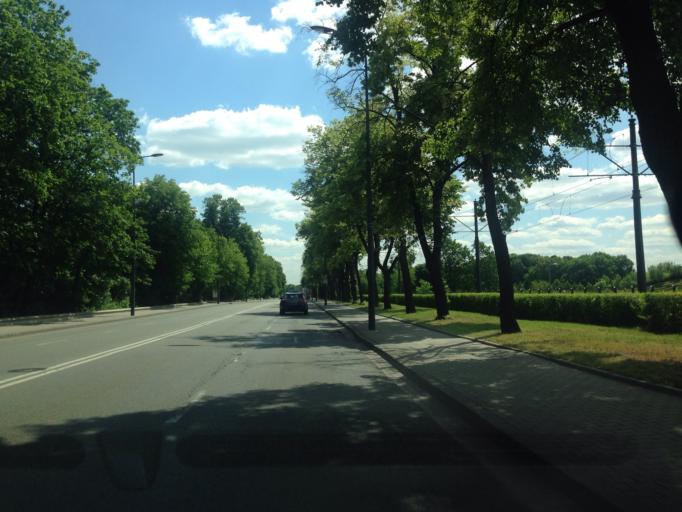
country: PL
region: Masovian Voivodeship
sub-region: Warszawa
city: Praga Polnoc
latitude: 52.2428
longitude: 21.0495
